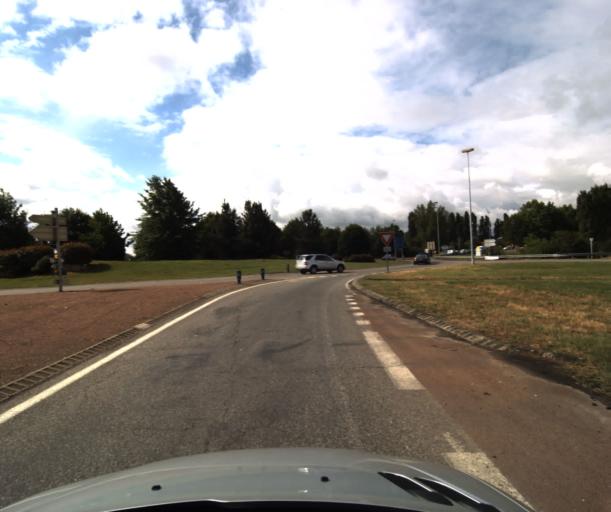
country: FR
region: Midi-Pyrenees
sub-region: Departement du Tarn-et-Garonne
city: Castelsarrasin
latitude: 44.0574
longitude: 1.0989
